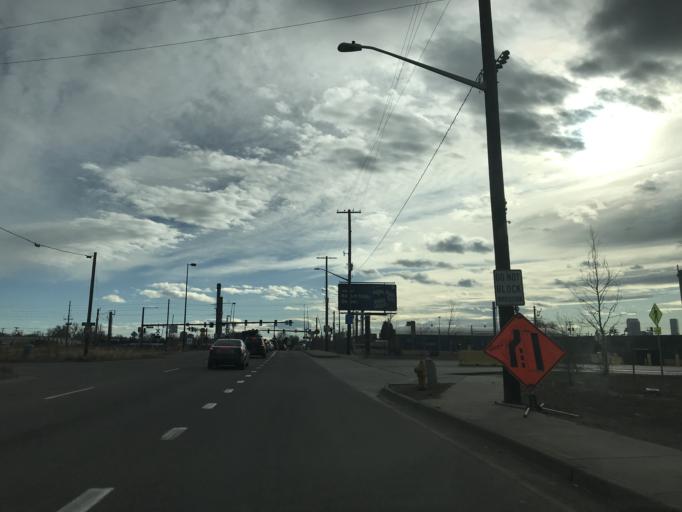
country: US
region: Colorado
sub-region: Adams County
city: Commerce City
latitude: 39.7743
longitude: -104.9595
